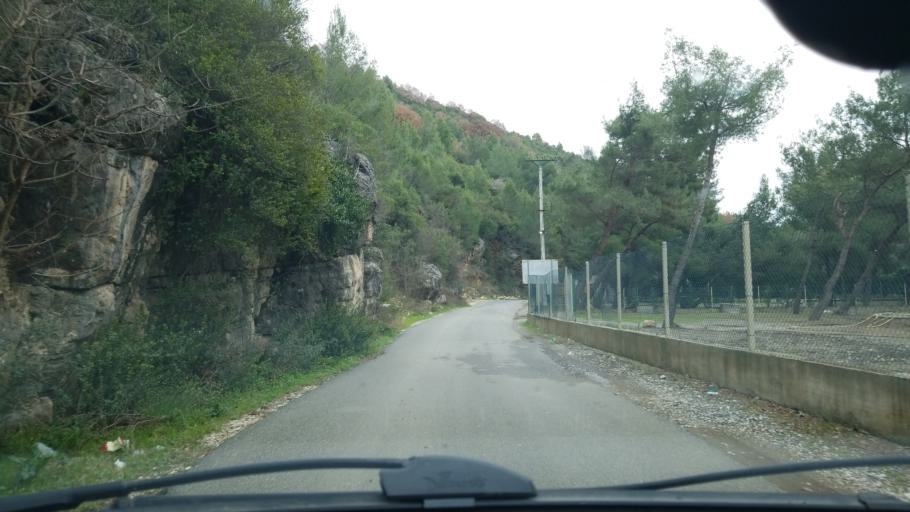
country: AL
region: Lezhe
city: Shengjin
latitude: 41.8205
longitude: 19.5635
